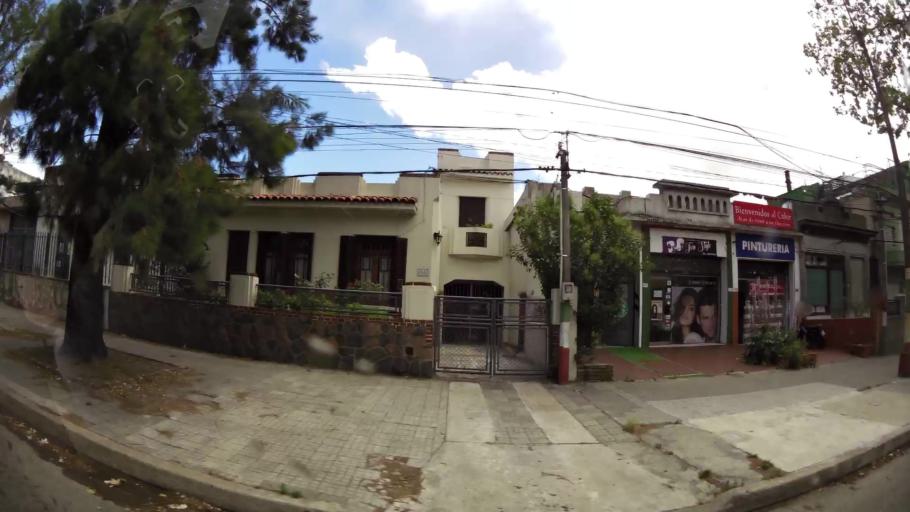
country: UY
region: Montevideo
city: Montevideo
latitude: -34.8691
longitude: -56.1816
